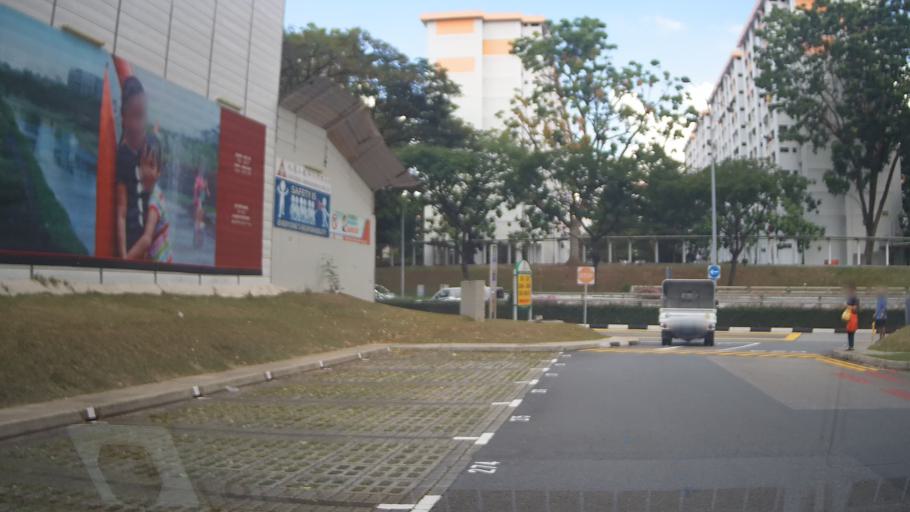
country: SG
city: Singapore
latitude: 1.3212
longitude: 103.7635
